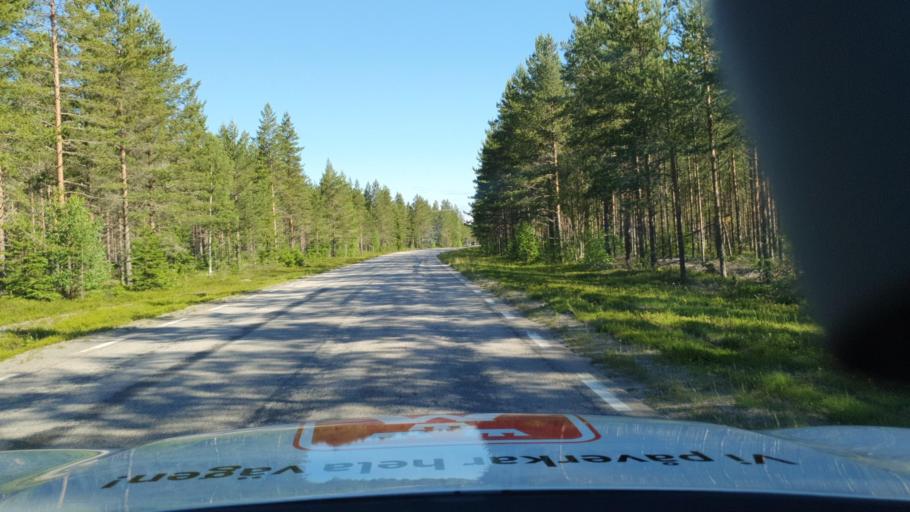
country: SE
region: Vaesterbotten
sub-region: Umea Kommun
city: Roback
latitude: 63.8596
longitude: 20.1445
